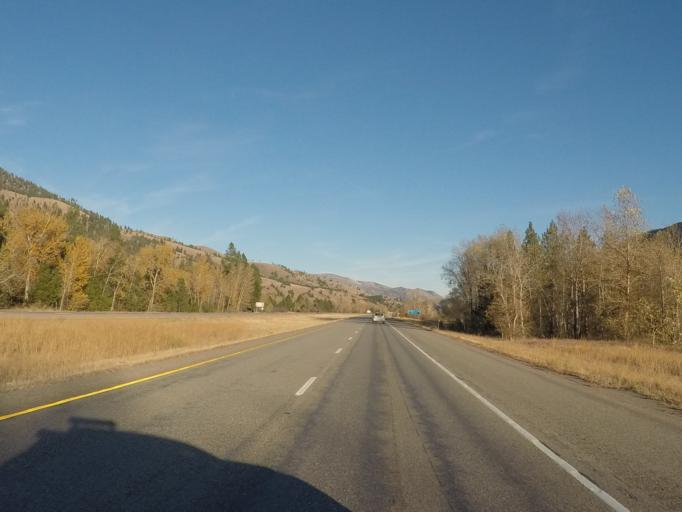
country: US
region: Montana
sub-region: Missoula County
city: Clinton
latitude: 46.7272
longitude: -113.6559
